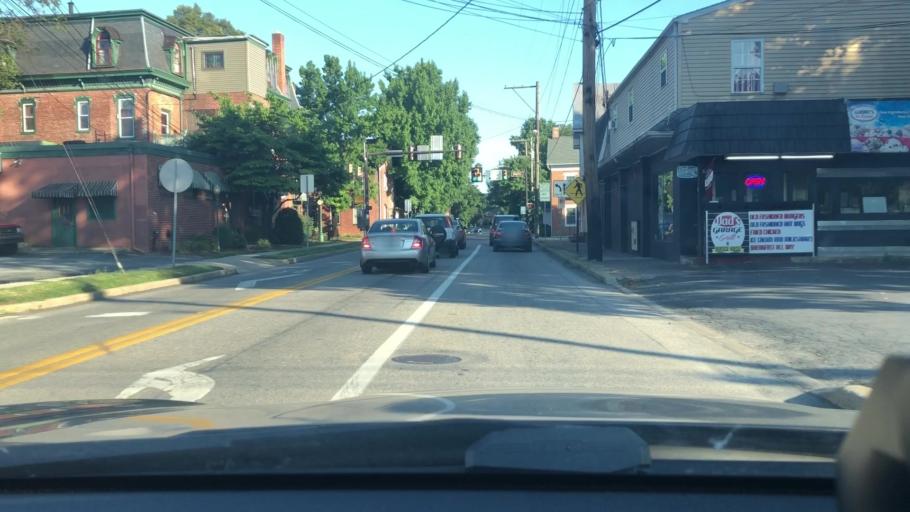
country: US
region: Pennsylvania
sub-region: Cumberland County
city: Mechanicsburg
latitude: 40.2153
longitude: -77.0032
